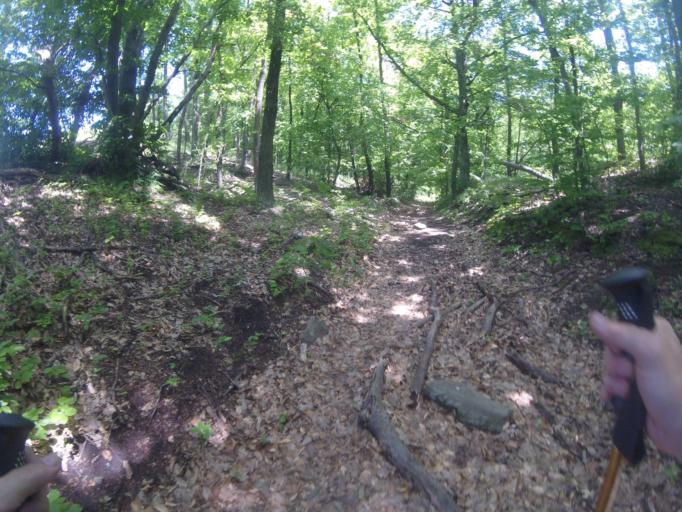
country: HU
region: Nograd
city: Batonyterenye
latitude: 47.9230
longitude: 19.8168
